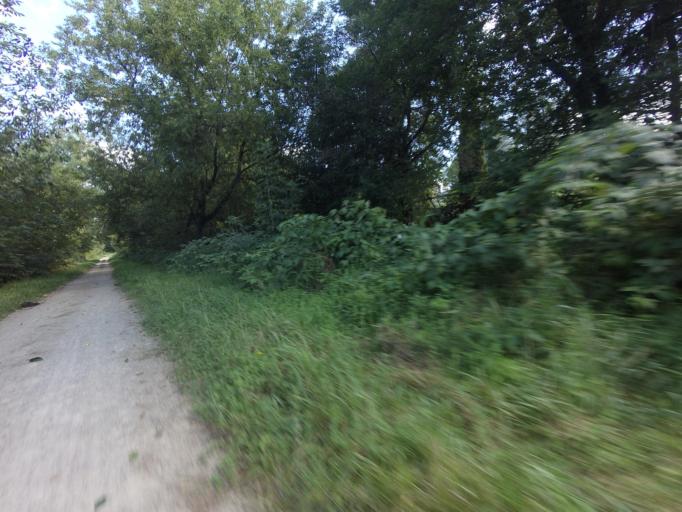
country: CA
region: Ontario
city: Orangeville
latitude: 43.7911
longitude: -80.3140
